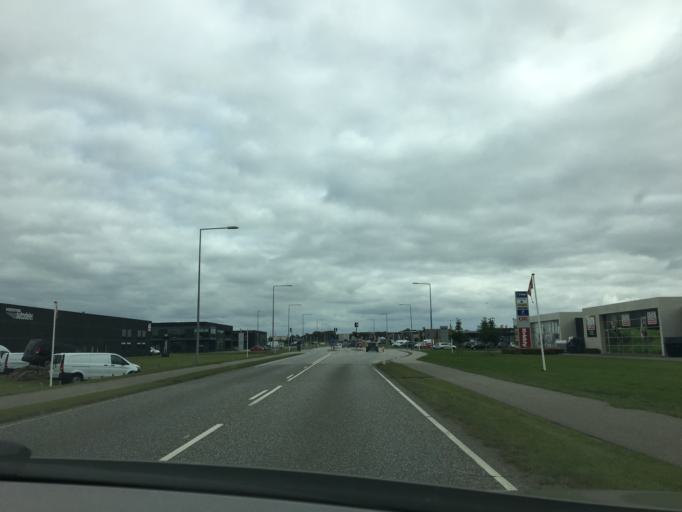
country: DK
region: Central Jutland
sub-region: Ringkobing-Skjern Kommune
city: Ringkobing
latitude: 56.0870
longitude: 8.2700
